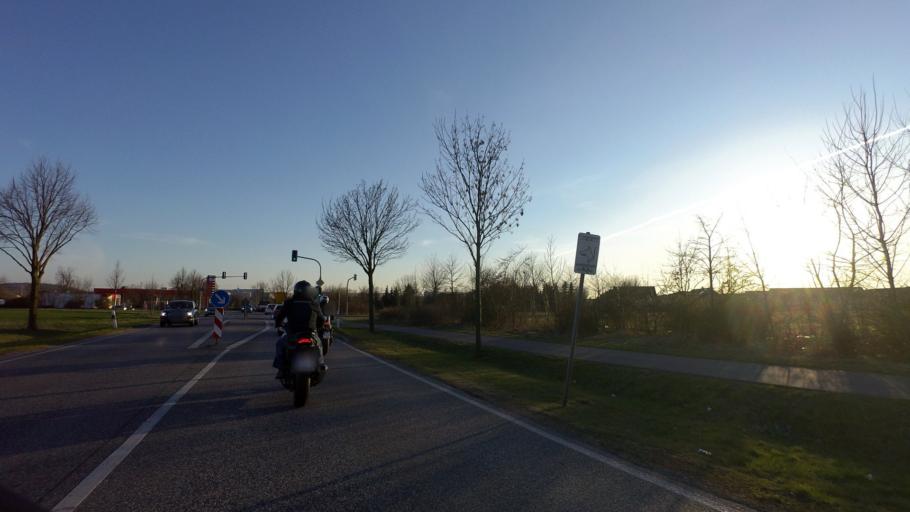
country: DE
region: Brandenburg
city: Ahrensfelde
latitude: 52.5789
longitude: 13.5850
